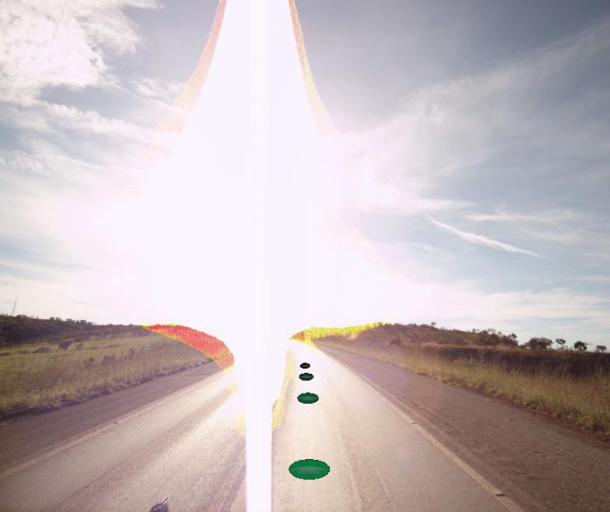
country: BR
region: Federal District
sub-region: Brasilia
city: Brasilia
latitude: -15.7538
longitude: -48.4163
